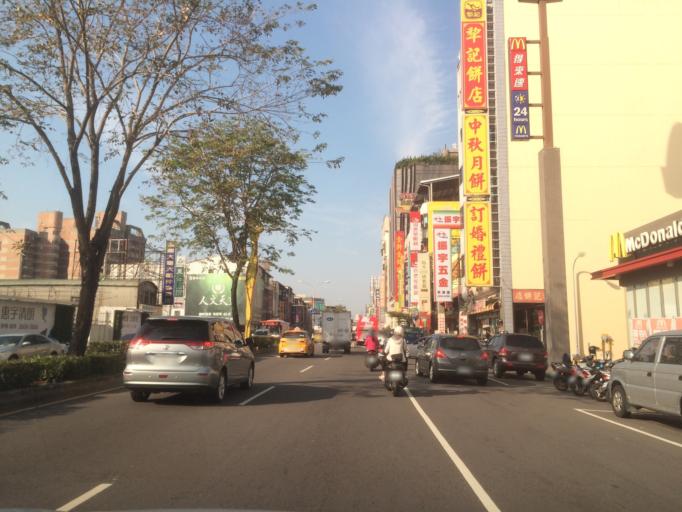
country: TW
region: Taiwan
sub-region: Taichung City
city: Taichung
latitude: 24.1707
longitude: 120.6722
